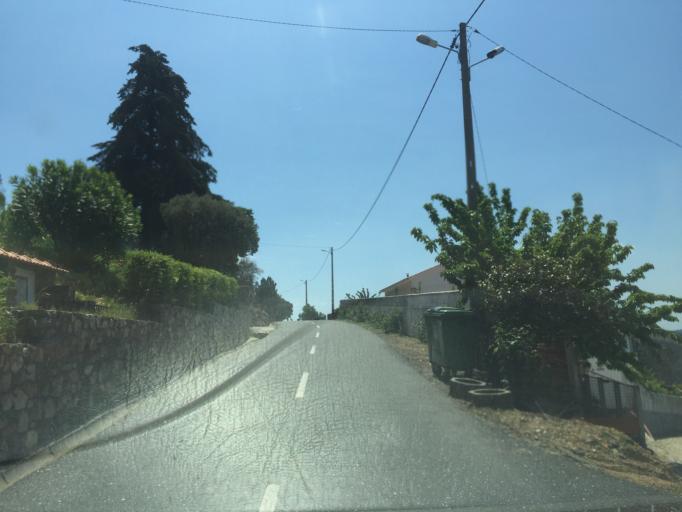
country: PT
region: Coimbra
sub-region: Pampilhosa da Serra
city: Pampilhosa da Serra
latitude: 40.0895
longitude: -7.8780
